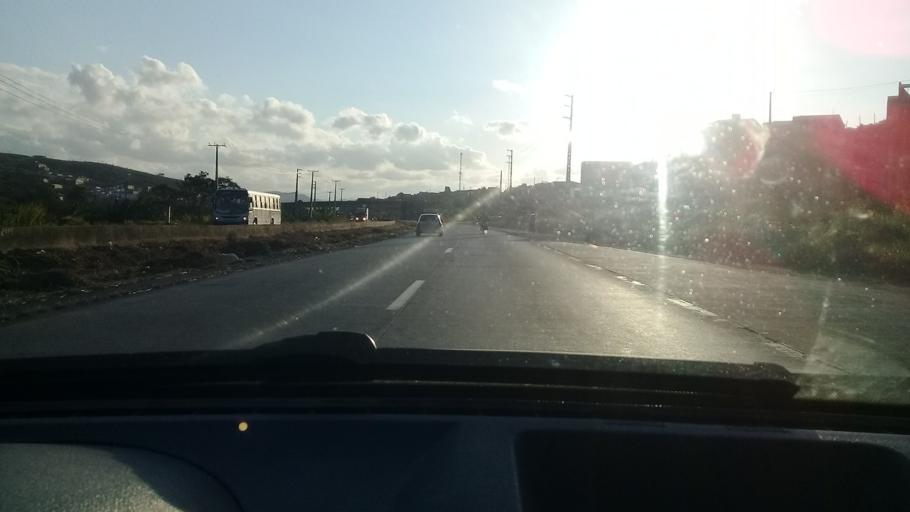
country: BR
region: Pernambuco
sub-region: Vitoria De Santo Antao
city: Vitoria de Santo Antao
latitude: -8.1261
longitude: -35.2778
